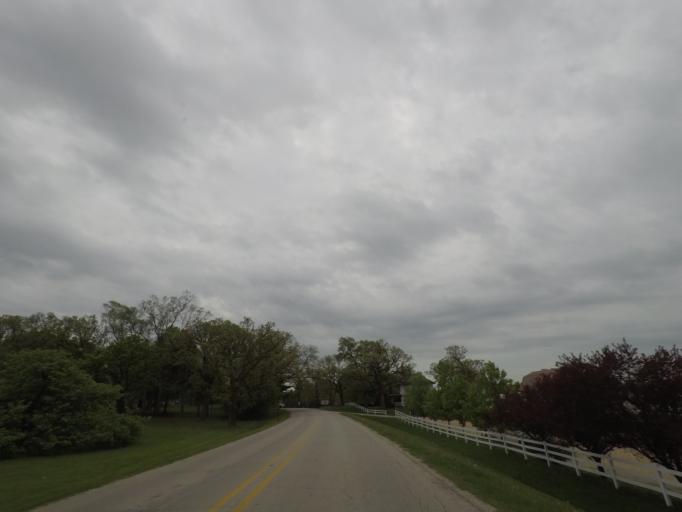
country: US
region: Illinois
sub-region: Winnebago County
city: Roscoe
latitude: 42.4393
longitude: -88.9863
